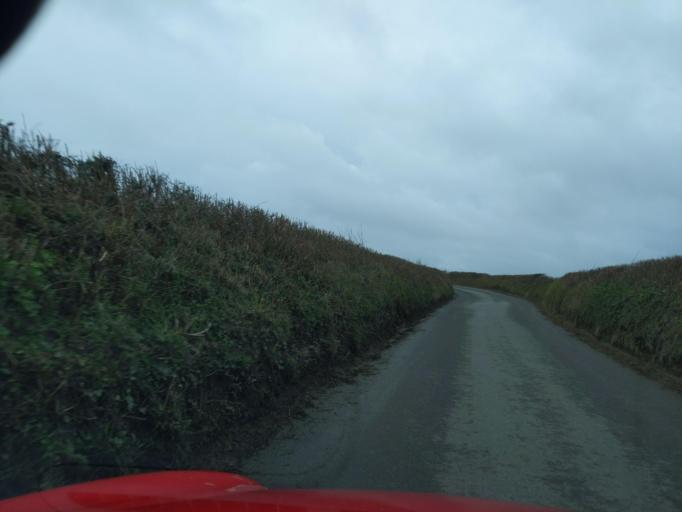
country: GB
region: England
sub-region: Devon
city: Modbury
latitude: 50.3276
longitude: -3.8827
